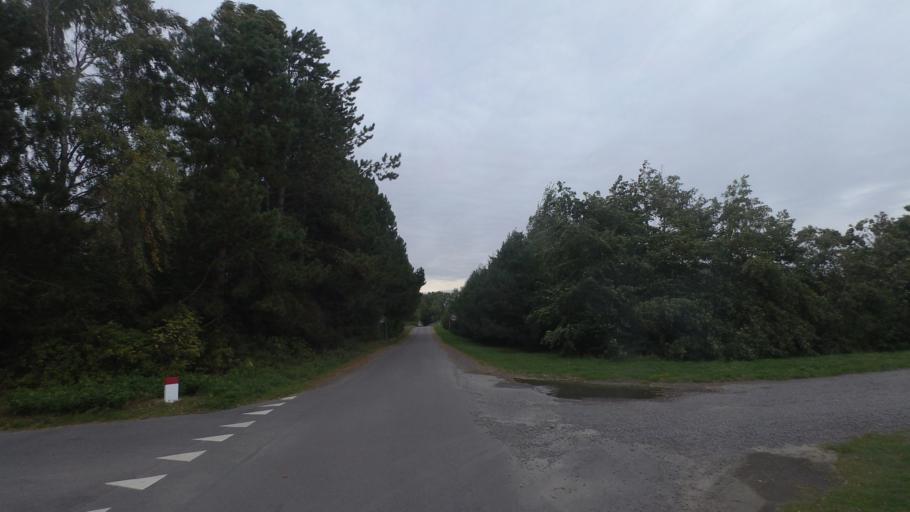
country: DK
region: Capital Region
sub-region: Bornholm Kommune
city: Akirkeby
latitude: 55.0027
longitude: 14.9919
